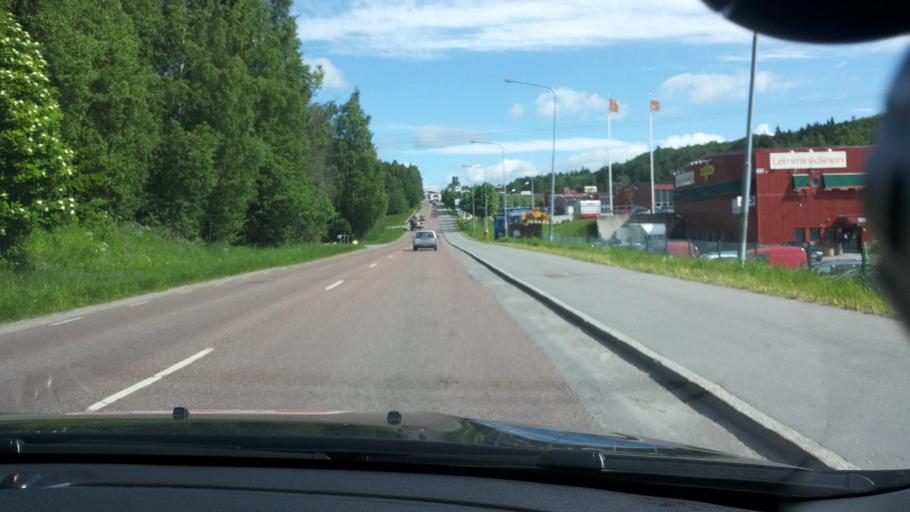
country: SE
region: Vaesternorrland
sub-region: Sundsvalls Kommun
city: Johannedal
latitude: 62.4199
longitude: 17.3440
